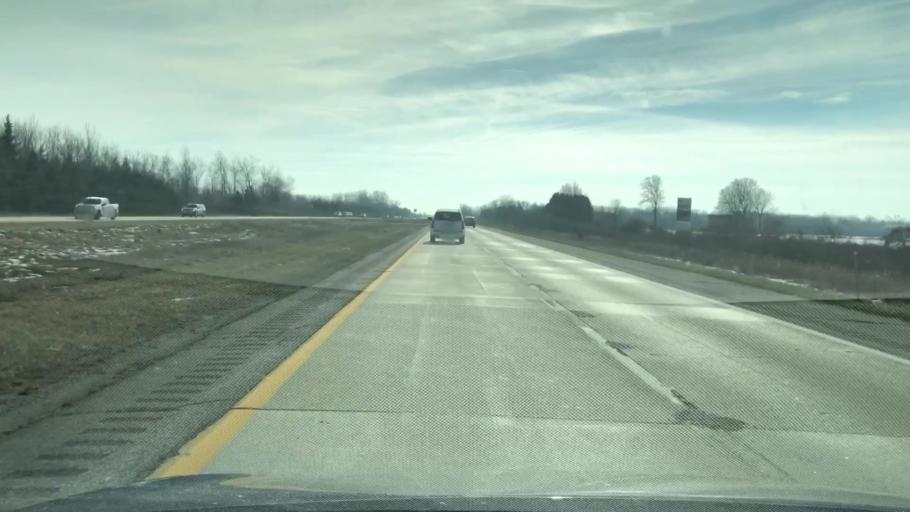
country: US
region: Michigan
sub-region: Bay County
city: Auburn
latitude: 43.7058
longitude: -84.0126
